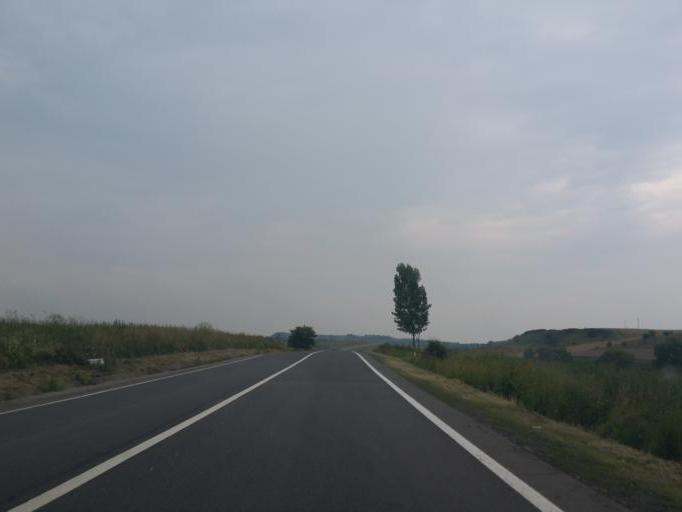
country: RO
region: Cluj
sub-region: Comuna Sanpaul
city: Sanpaul
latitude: 46.9194
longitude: 23.4198
